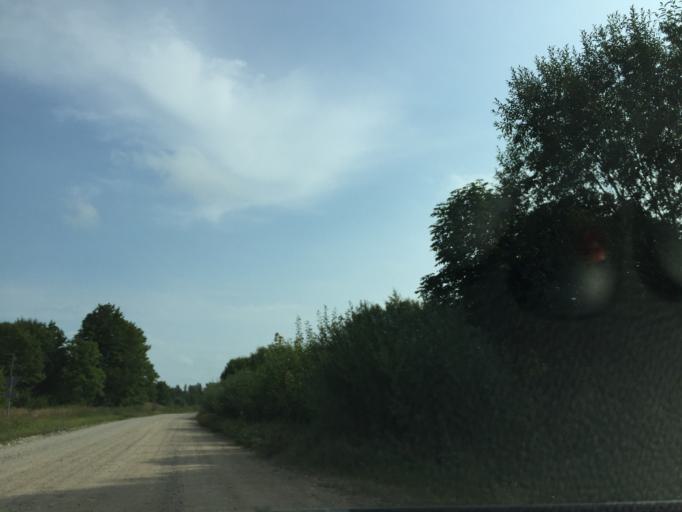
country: LV
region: Ludzas Rajons
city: Ludza
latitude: 56.2864
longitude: 27.7543
